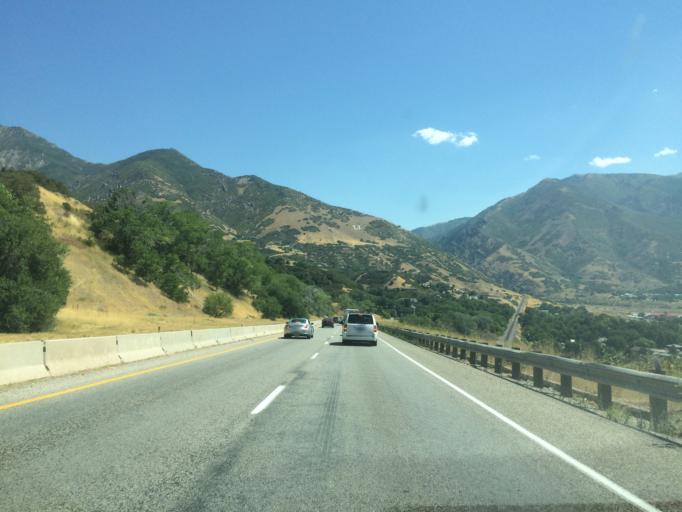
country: US
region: Utah
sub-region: Weber County
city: Uintah
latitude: 41.1477
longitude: -111.9275
